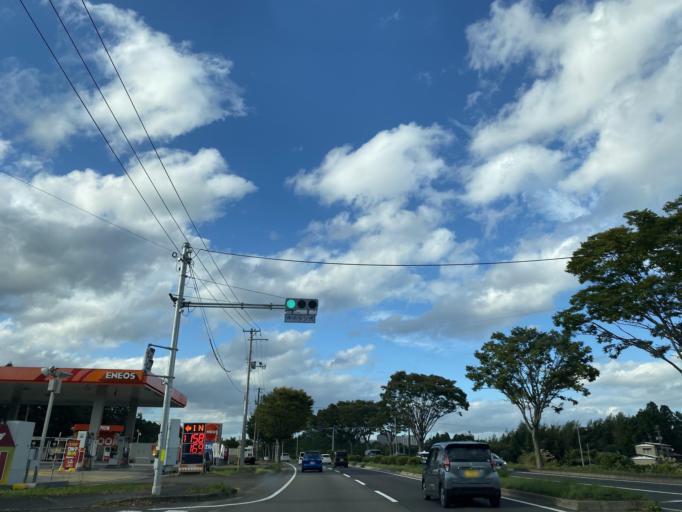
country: JP
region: Miyagi
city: Sendai-shi
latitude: 38.3241
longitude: 140.8442
